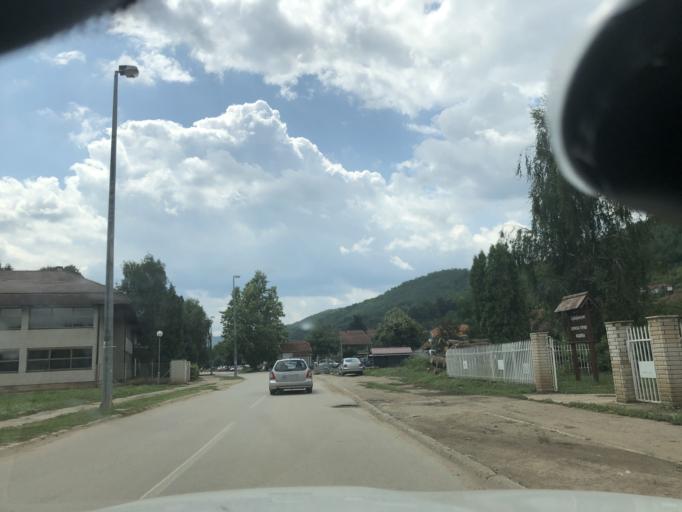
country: RS
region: Central Serbia
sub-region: Jablanicki Okrug
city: Medvega
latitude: 42.8407
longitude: 21.5862
